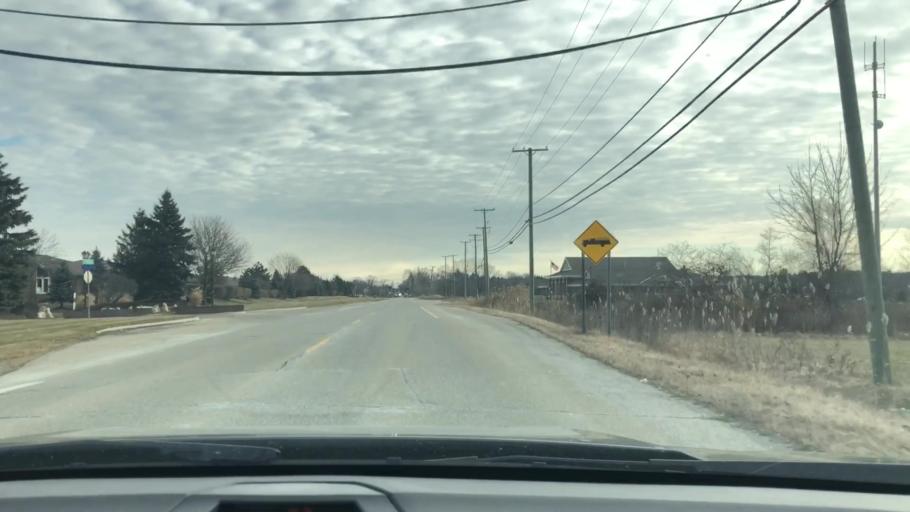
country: US
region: Michigan
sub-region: Macomb County
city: Shelby
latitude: 42.7284
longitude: -83.0243
